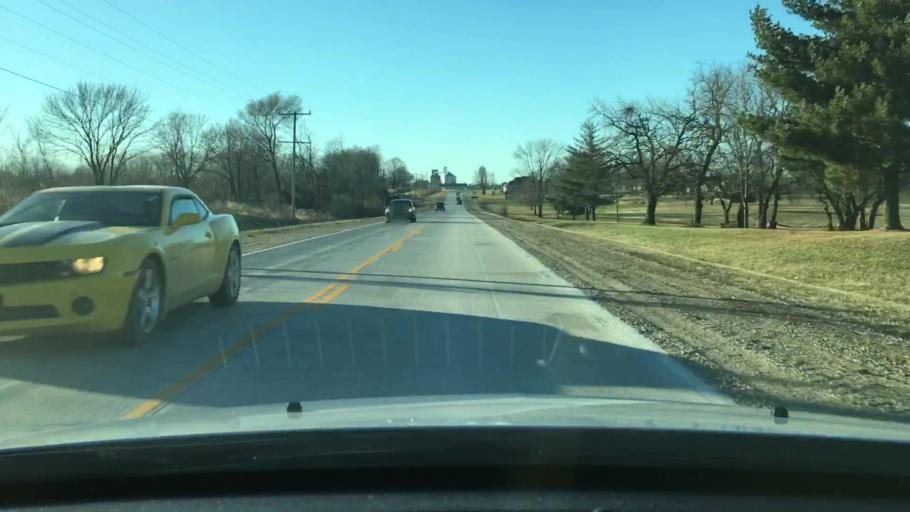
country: US
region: Missouri
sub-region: Boone County
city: Centralia
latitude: 39.2093
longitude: -92.1122
